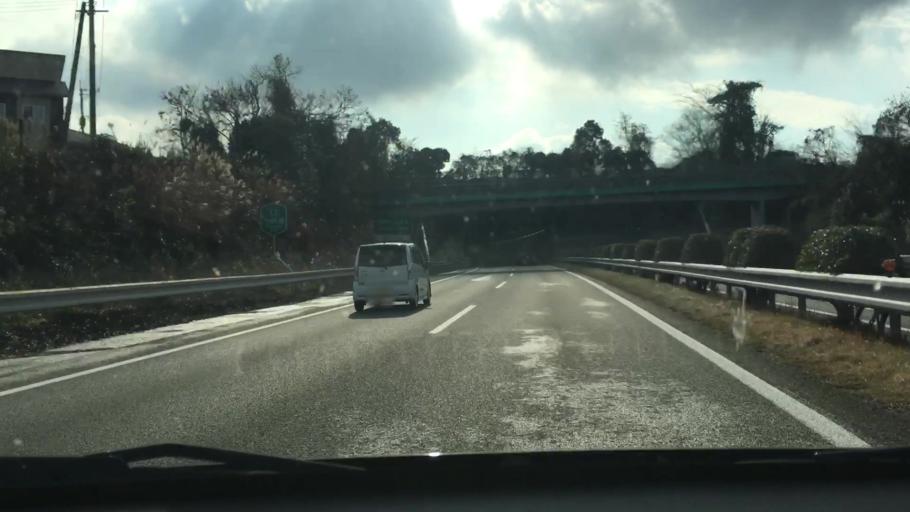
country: JP
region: Kumamoto
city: Uto
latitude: 32.6915
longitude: 130.7387
